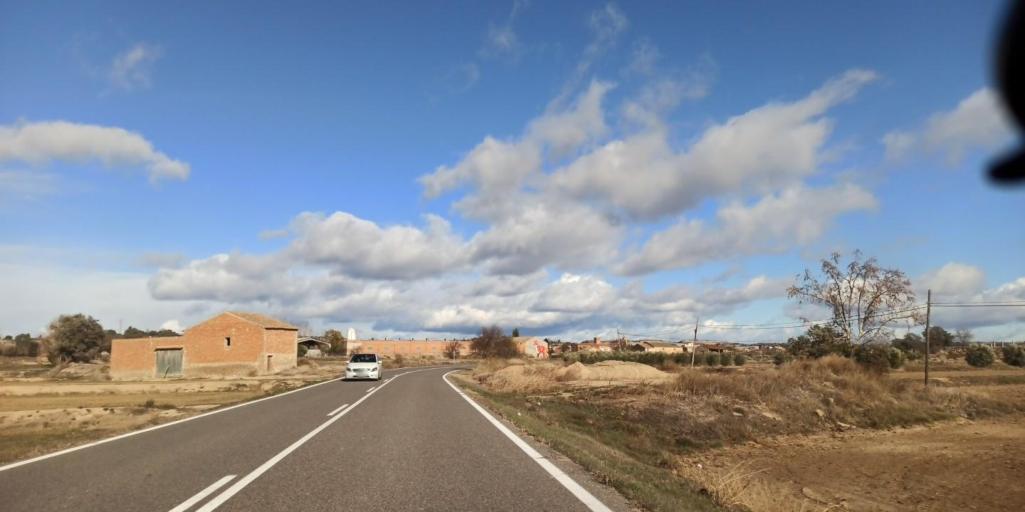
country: ES
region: Catalonia
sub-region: Provincia de Lleida
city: Penelles
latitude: 41.7519
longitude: 0.9556
